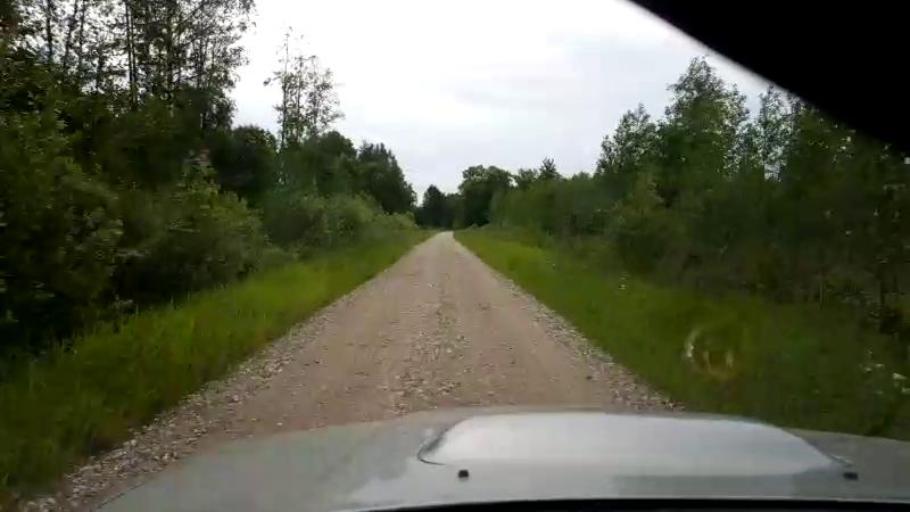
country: EE
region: Paernumaa
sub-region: Tootsi vald
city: Tootsi
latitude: 58.5514
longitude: 24.7450
